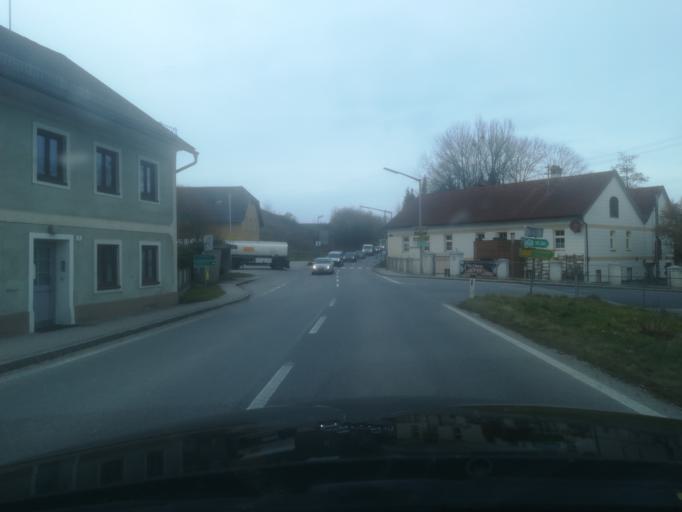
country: AT
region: Upper Austria
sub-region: Wels-Land
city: Gunskirchen
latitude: 48.0869
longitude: 13.9474
